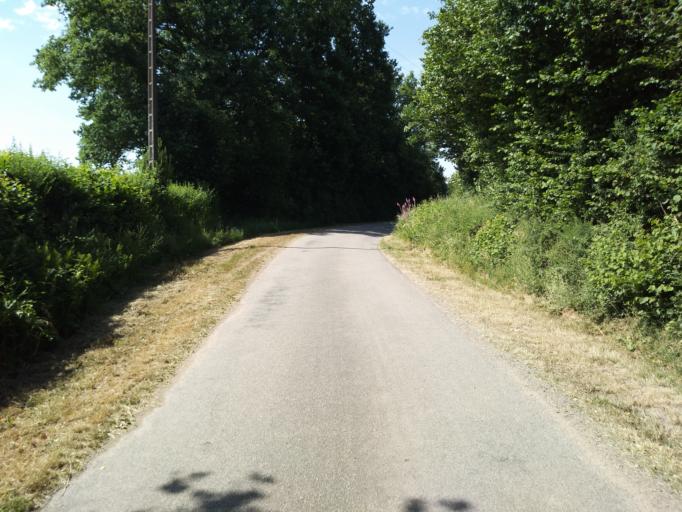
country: FR
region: Bourgogne
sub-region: Departement de la Cote-d'Or
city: Saulieu
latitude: 47.2886
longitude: 4.1325
